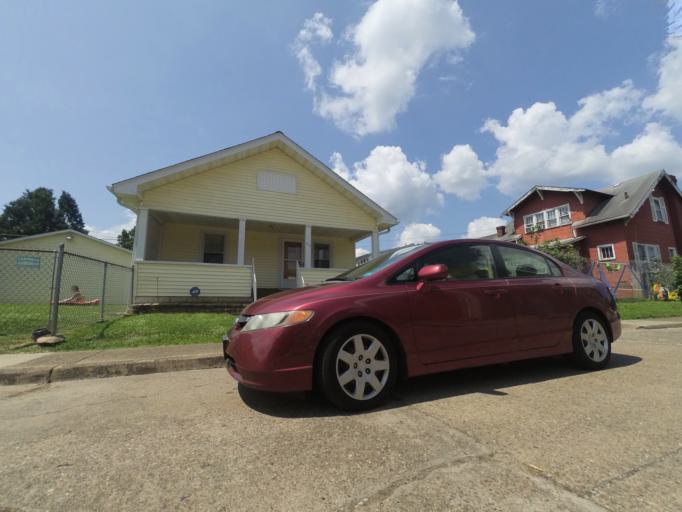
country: US
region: West Virginia
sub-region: Cabell County
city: Huntington
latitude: 38.4129
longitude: -82.4603
